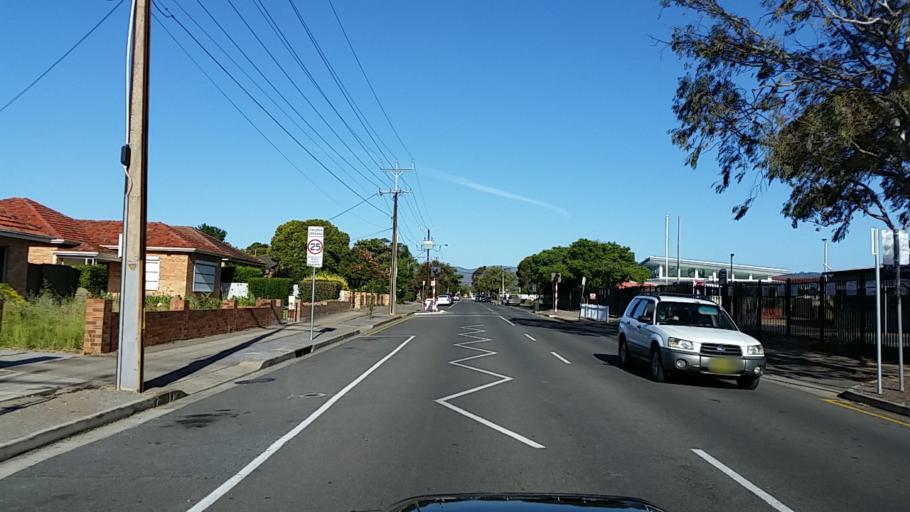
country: AU
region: South Australia
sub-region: Marion
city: South Plympton
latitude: -34.9772
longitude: 138.5569
